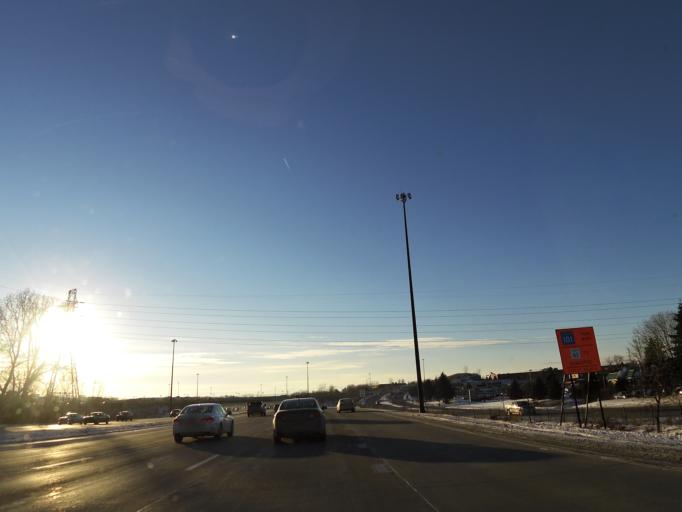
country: US
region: Minnesota
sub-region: Hennepin County
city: Eden Prairie
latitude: 44.8636
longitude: -93.4382
